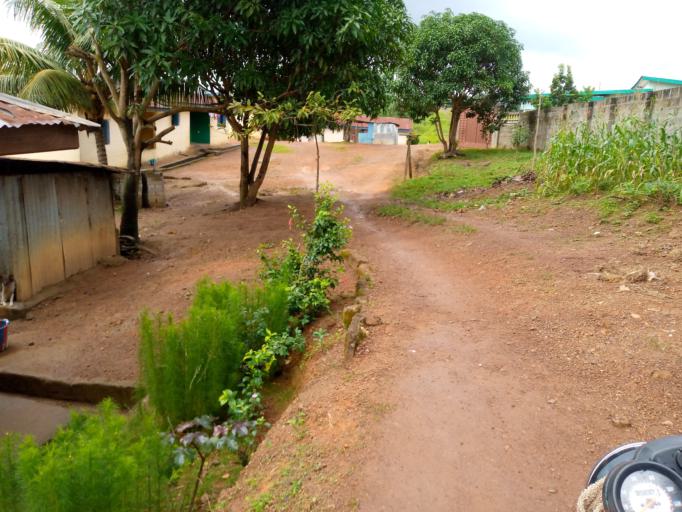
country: SL
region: Eastern Province
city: Kenema
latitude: 7.8751
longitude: -11.1727
